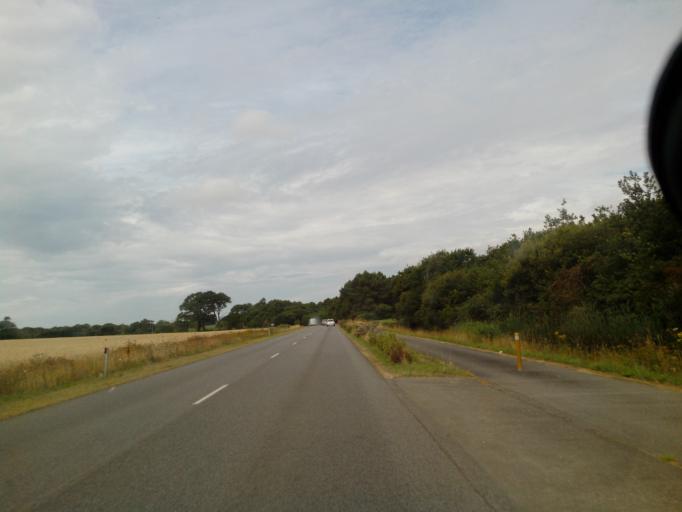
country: FR
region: Brittany
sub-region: Departement du Morbihan
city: Erdeven
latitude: 47.6432
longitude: -3.1239
